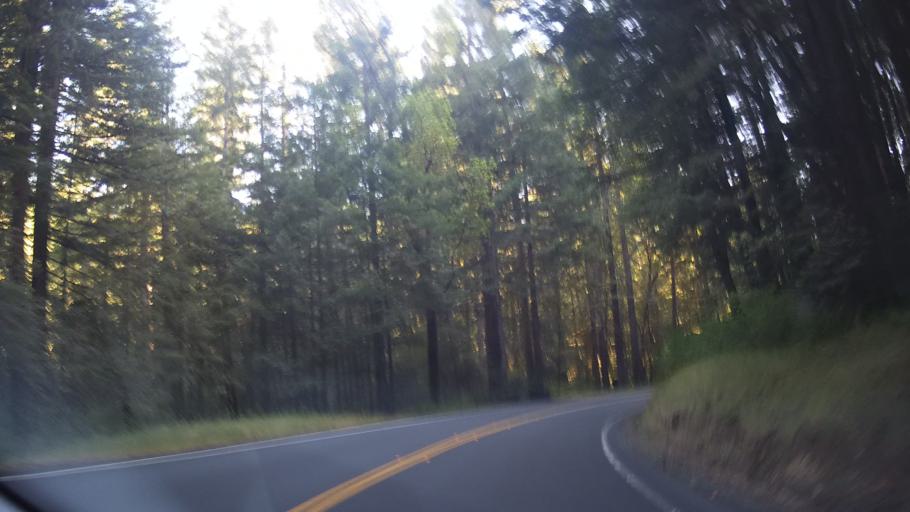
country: US
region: California
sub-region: Mendocino County
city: Brooktrails
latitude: 39.3477
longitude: -123.5621
